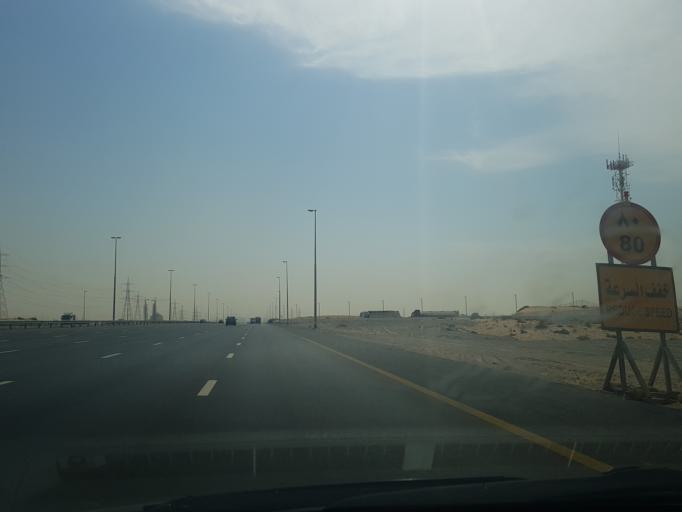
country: AE
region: Ash Shariqah
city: Sharjah
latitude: 25.2557
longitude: 55.5739
